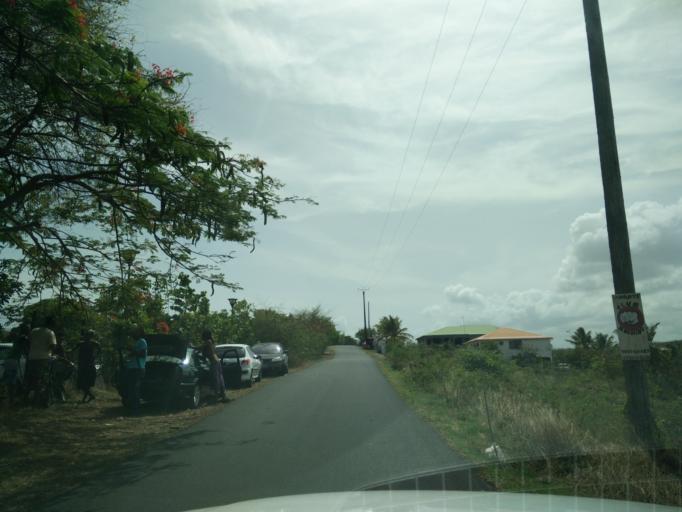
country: GP
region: Guadeloupe
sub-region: Guadeloupe
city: Sainte-Anne
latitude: 16.2432
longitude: -61.3304
